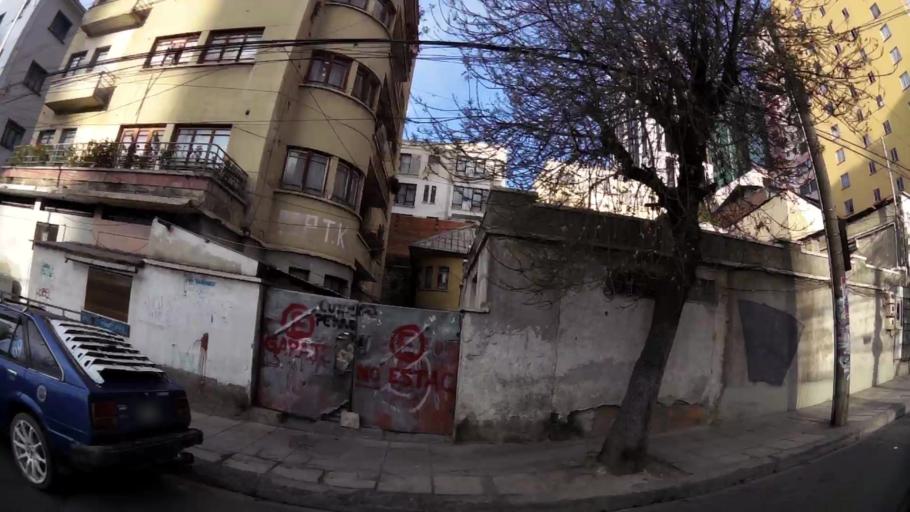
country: BO
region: La Paz
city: La Paz
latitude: -16.5133
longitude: -68.1221
